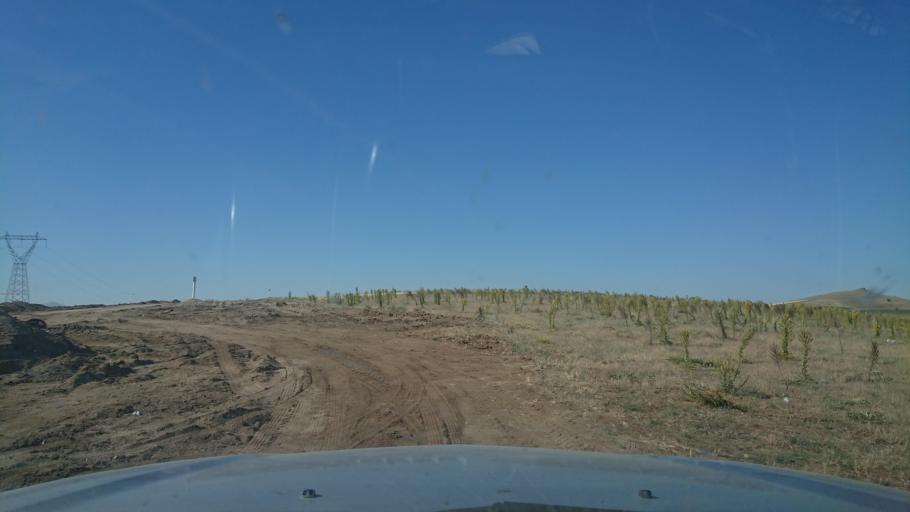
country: TR
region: Aksaray
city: Agacoren
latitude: 38.8426
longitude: 33.9439
